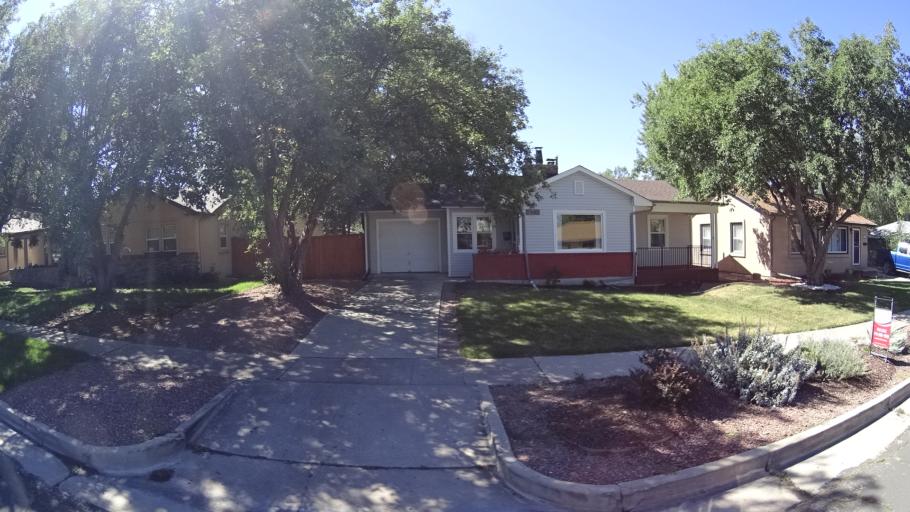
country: US
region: Colorado
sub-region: El Paso County
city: Colorado Springs
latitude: 38.8533
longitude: -104.7982
